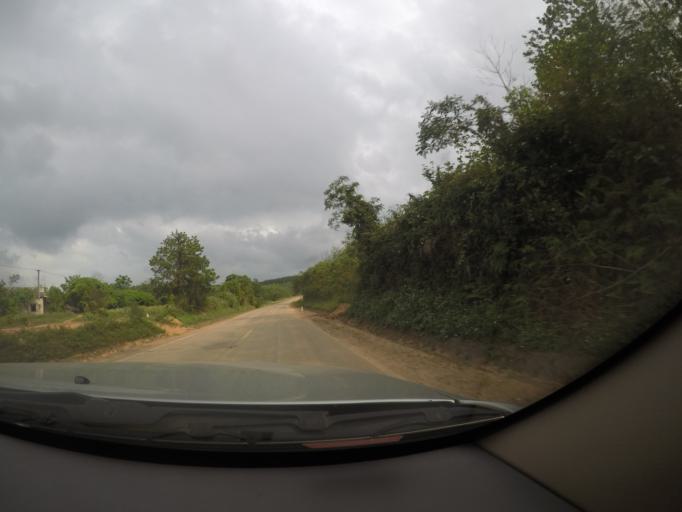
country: VN
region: Quang Tri
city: Ho Xa
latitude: 17.0453
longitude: 106.8808
